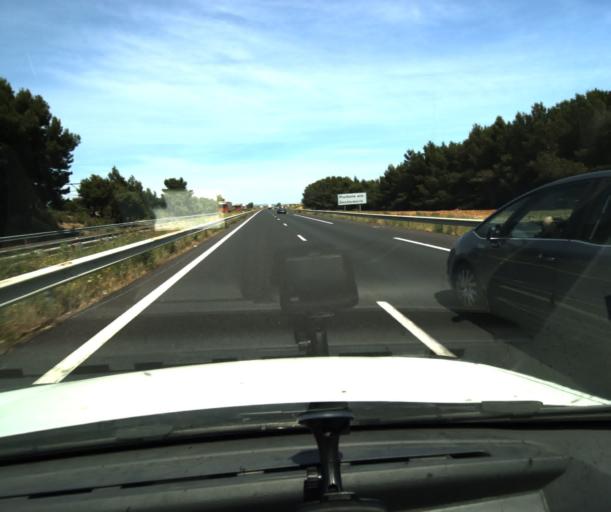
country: FR
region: Languedoc-Roussillon
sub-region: Departement des Pyrenees-Orientales
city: Perpignan
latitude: 42.7283
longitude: 2.8790
